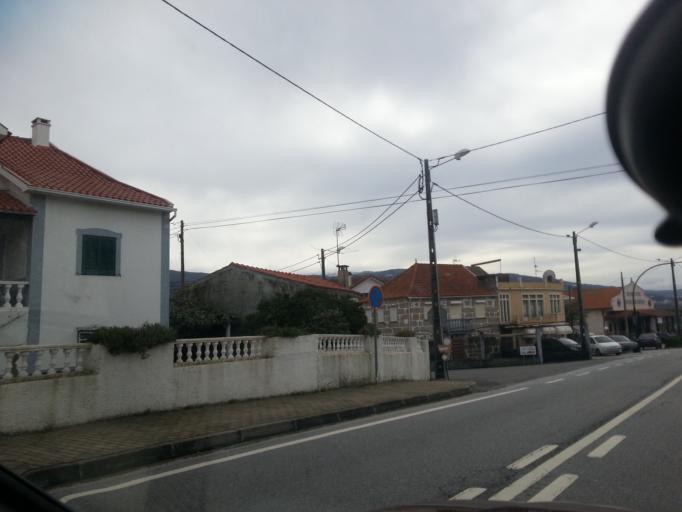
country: PT
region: Guarda
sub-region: Seia
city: Seia
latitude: 40.4666
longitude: -7.6838
